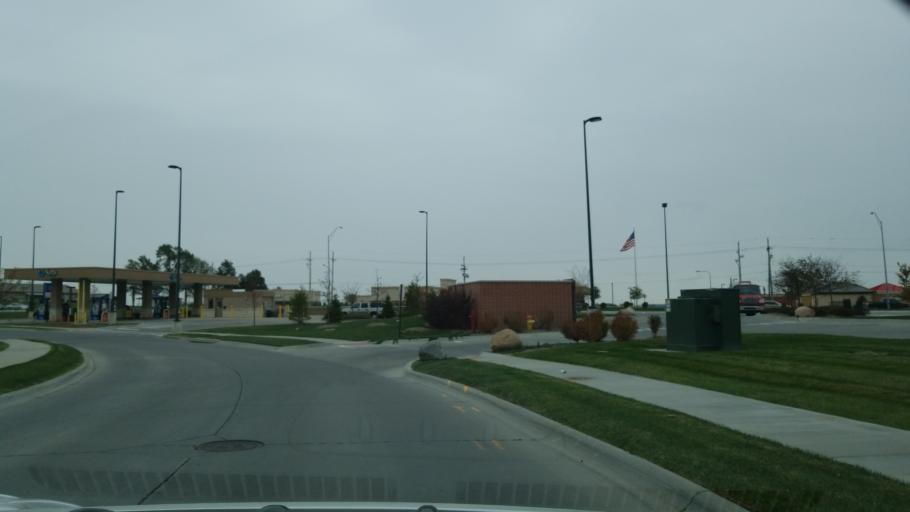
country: US
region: Nebraska
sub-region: Sarpy County
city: Papillion
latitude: 41.1627
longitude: -96.0225
